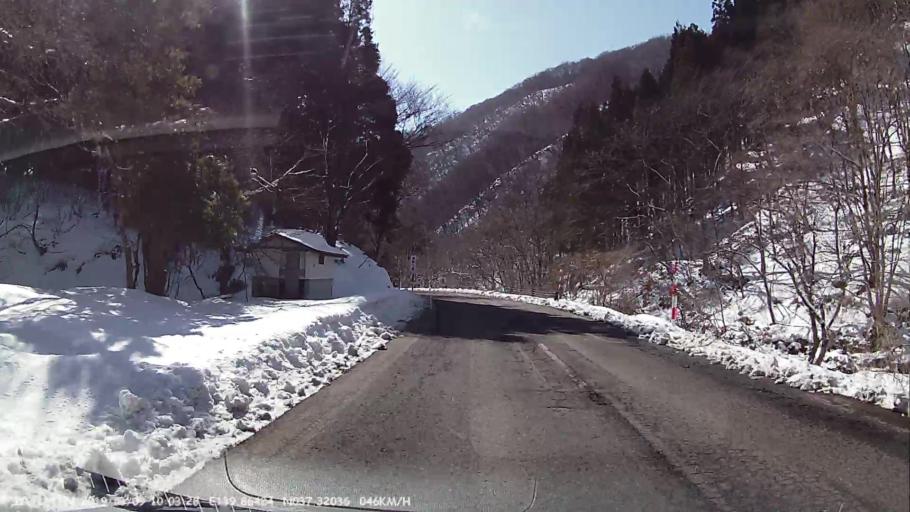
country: JP
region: Fukushima
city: Kitakata
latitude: 37.3204
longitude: 139.8642
